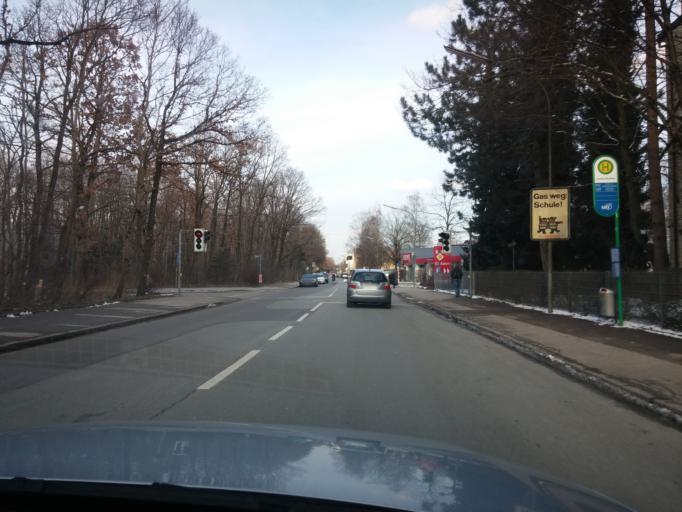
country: DE
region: Bavaria
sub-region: Upper Bavaria
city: Ottobrunn
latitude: 48.0699
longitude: 11.6816
